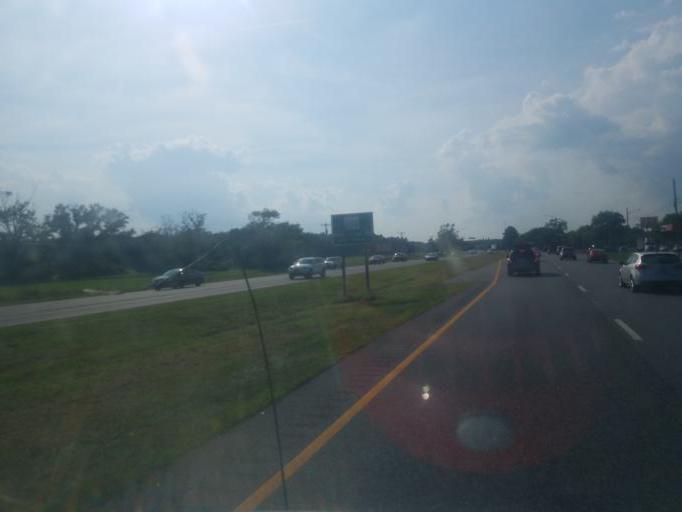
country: US
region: Maryland
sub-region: Worcester County
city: Ocean Pines
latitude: 38.3453
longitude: -75.1656
